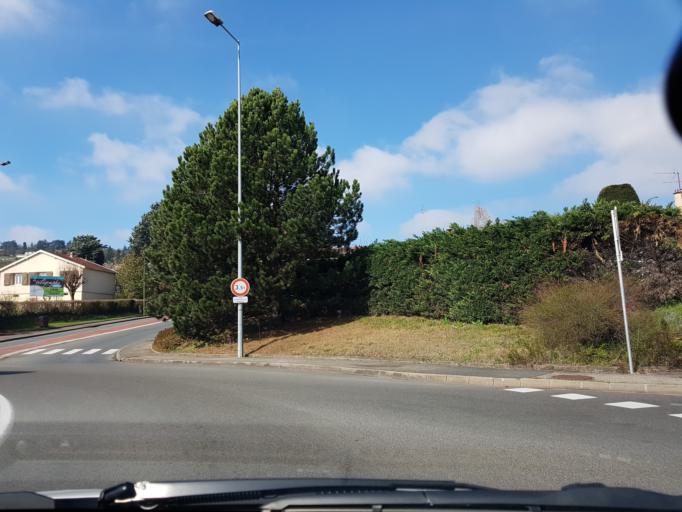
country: FR
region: Rhone-Alpes
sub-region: Departement du Rhone
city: Villefranche-sur-Saone
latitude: 45.9732
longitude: 4.7171
